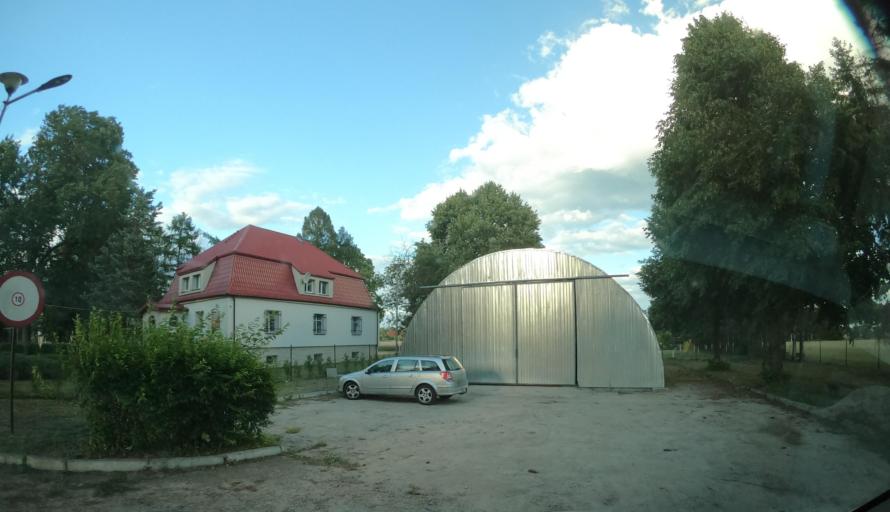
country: PL
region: West Pomeranian Voivodeship
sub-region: Powiat koszalinski
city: Polanow
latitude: 54.1245
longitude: 16.6624
